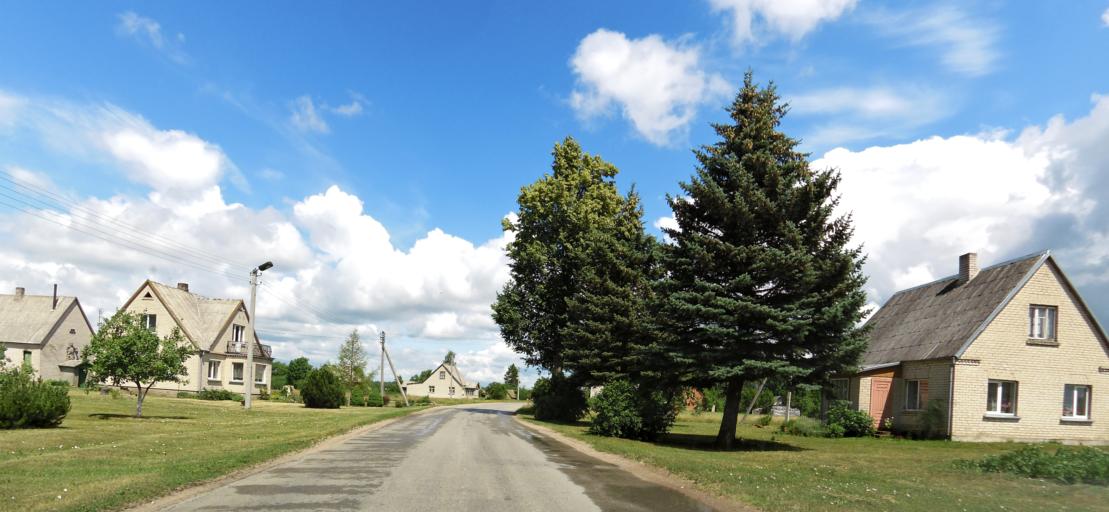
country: LT
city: Vabalninkas
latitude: 55.8860
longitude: 24.7864
